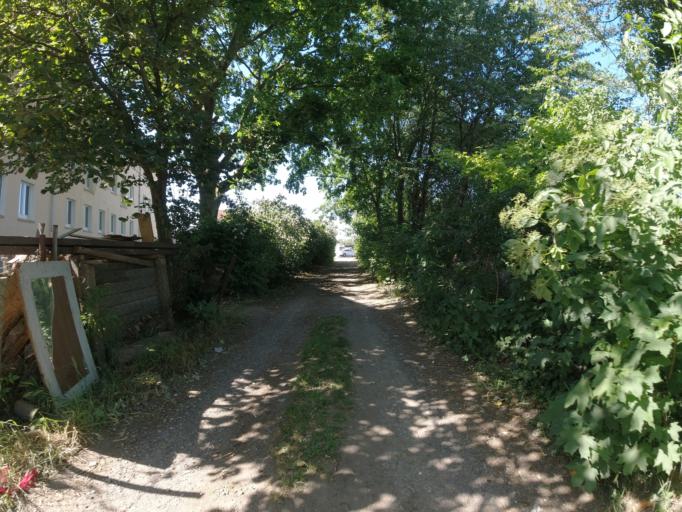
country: DE
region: North Rhine-Westphalia
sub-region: Regierungsbezirk Dusseldorf
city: Hochfeld
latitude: 51.3815
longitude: 6.6885
